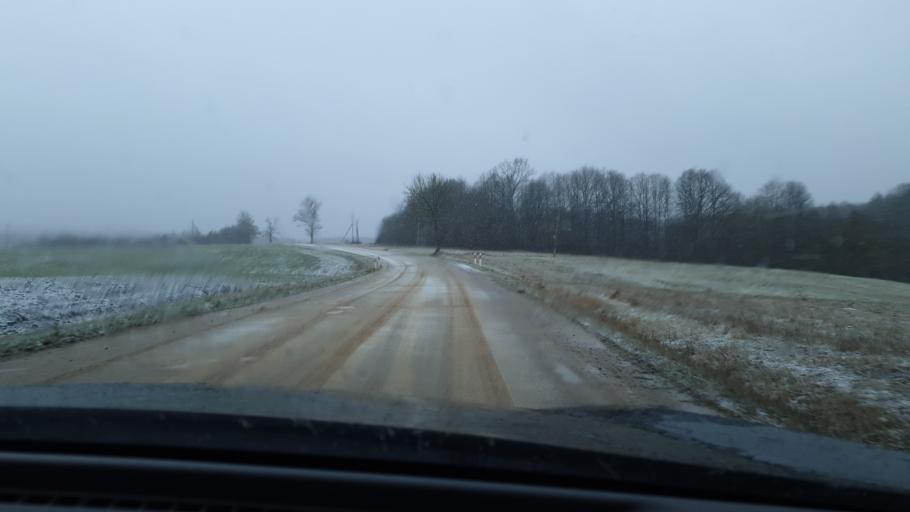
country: LT
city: Jieznas
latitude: 54.5594
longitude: 24.3169
